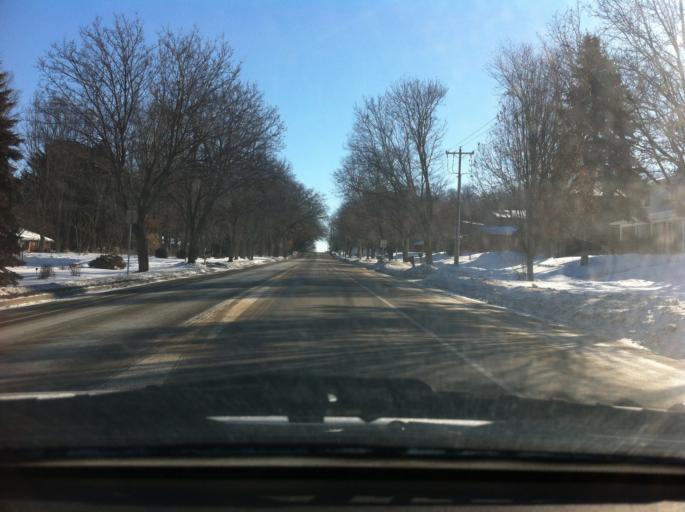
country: US
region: Wisconsin
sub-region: Dane County
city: Middleton
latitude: 43.0752
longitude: -89.4911
